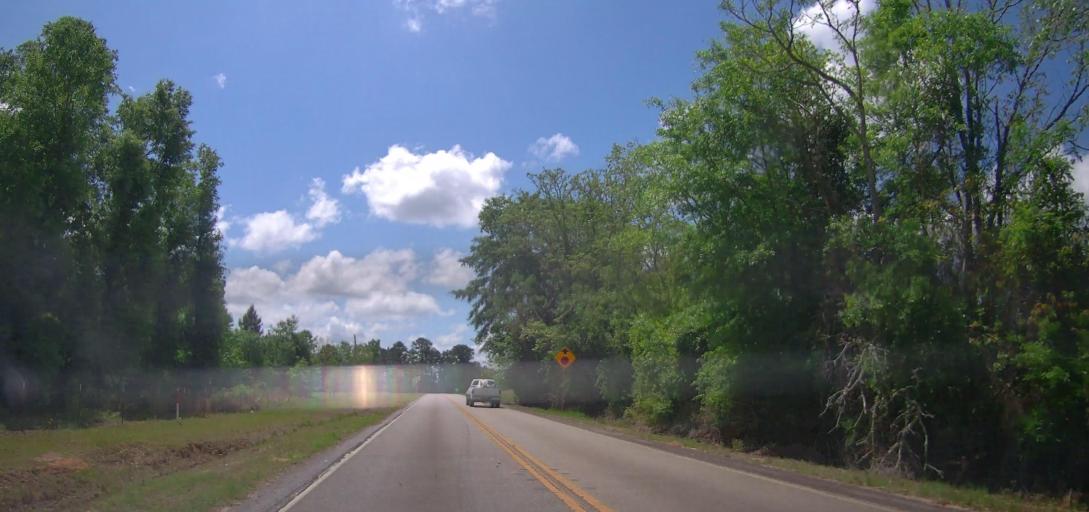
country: US
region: Georgia
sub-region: Bleckley County
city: Cochran
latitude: 32.4526
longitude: -83.2868
